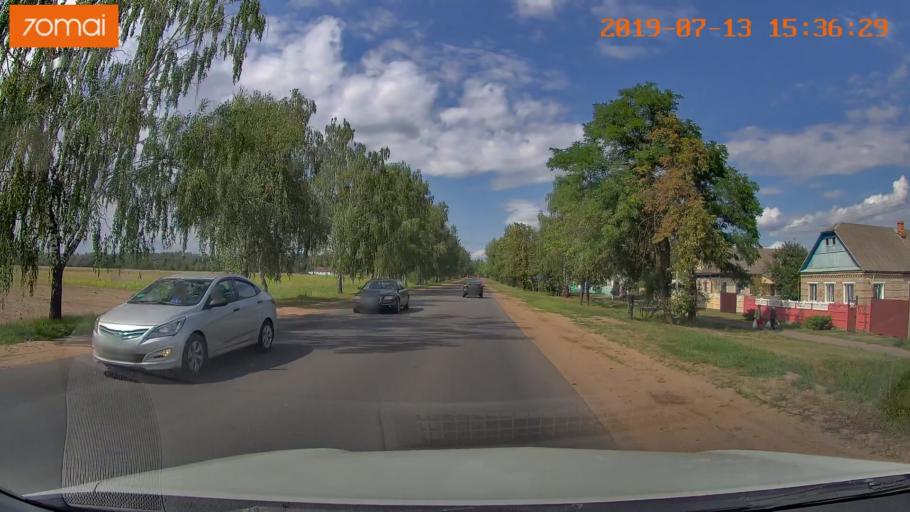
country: BY
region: Mogilev
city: Babruysk
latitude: 53.1319
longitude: 29.1666
